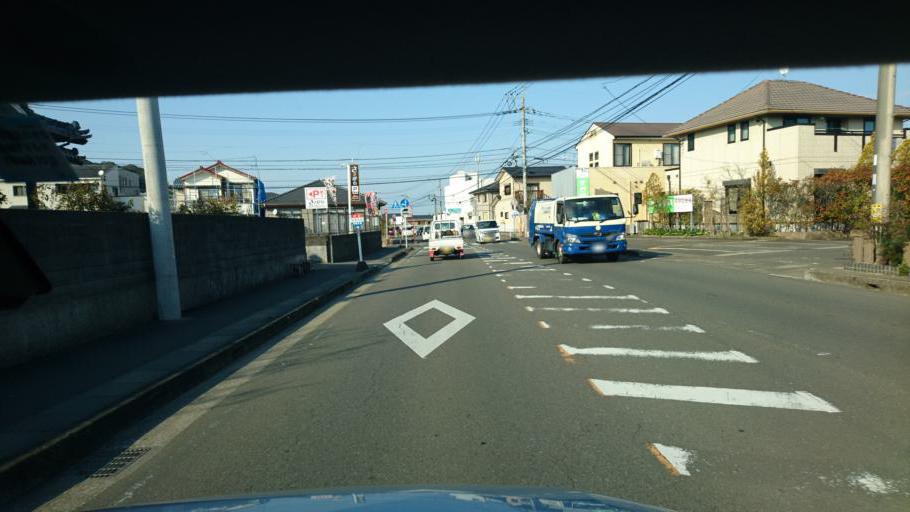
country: JP
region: Miyazaki
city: Miyazaki-shi
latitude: 31.9762
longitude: 131.4403
